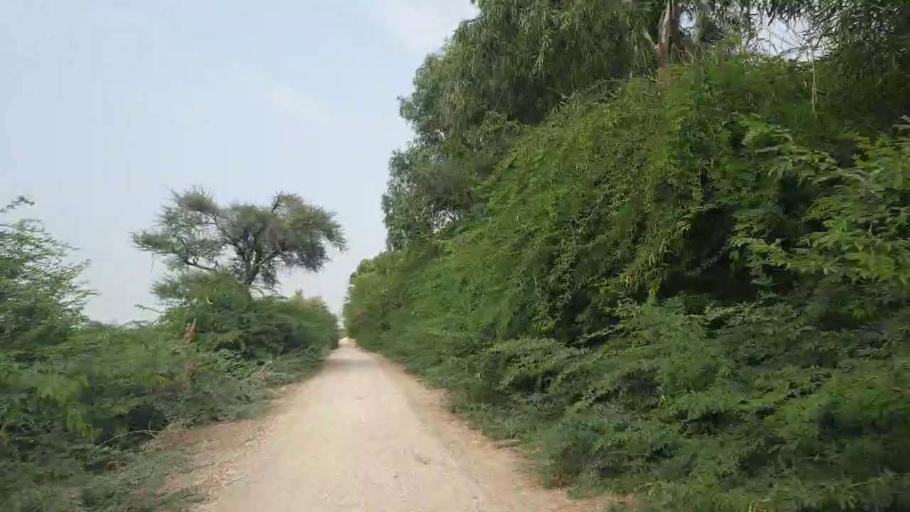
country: PK
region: Sindh
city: Badin
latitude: 24.5987
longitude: 68.7413
